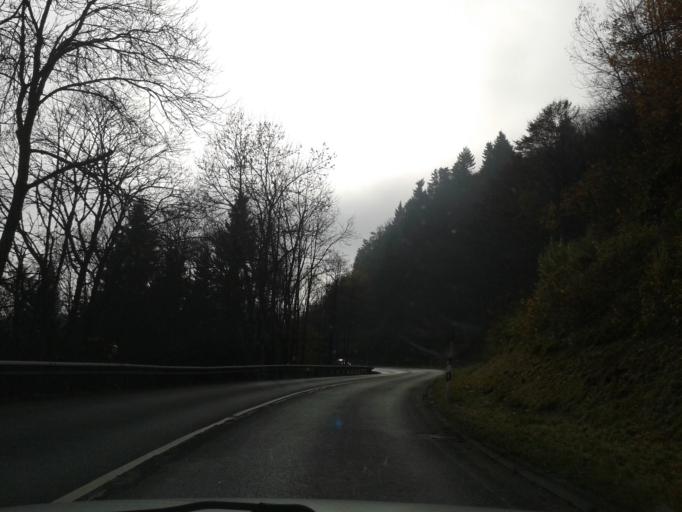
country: DE
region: North Rhine-Westphalia
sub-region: Regierungsbezirk Arnsberg
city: Winterberg
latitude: 51.1808
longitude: 8.4986
